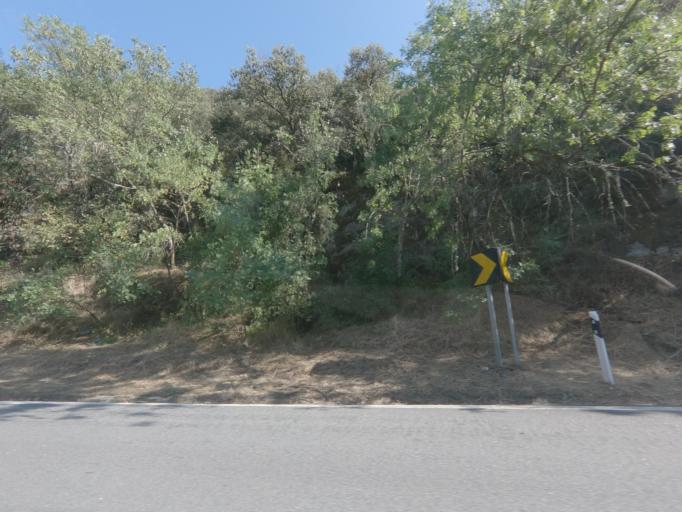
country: PT
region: Viseu
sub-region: Tabuaco
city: Tabuaco
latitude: 41.1520
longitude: -7.5835
